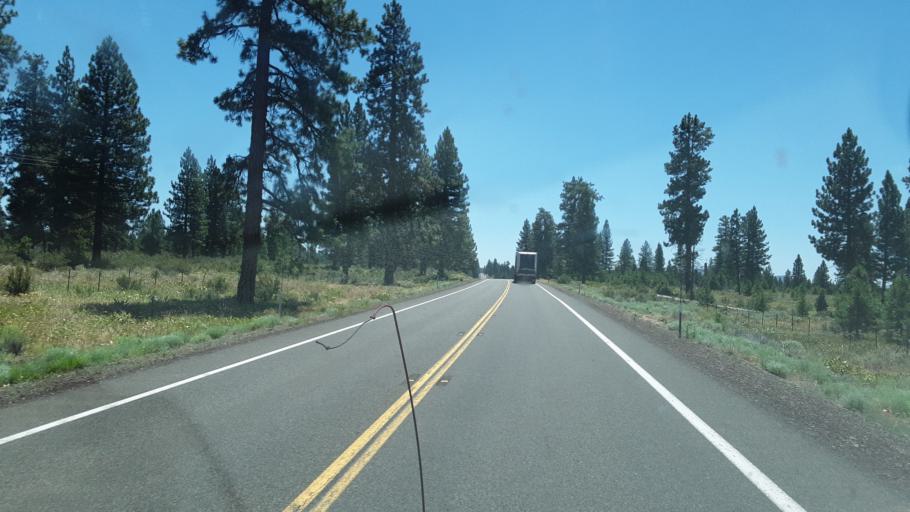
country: US
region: California
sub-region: Siskiyou County
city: Tulelake
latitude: 41.5804
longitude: -121.1893
